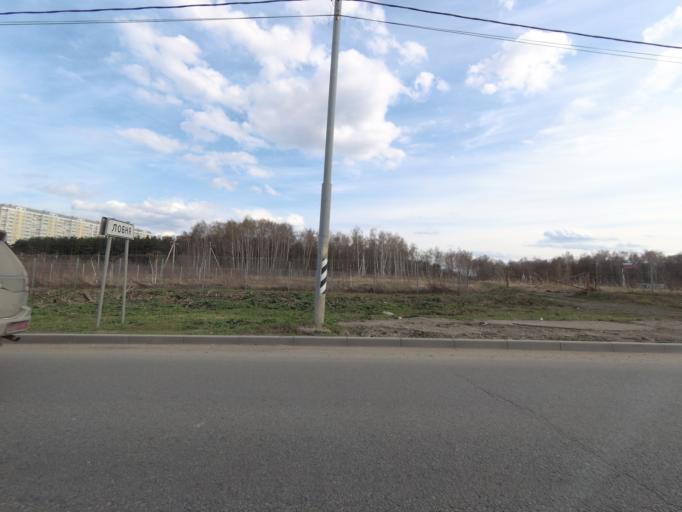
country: RU
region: Moskovskaya
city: Lobnya
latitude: 56.0050
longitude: 37.4311
